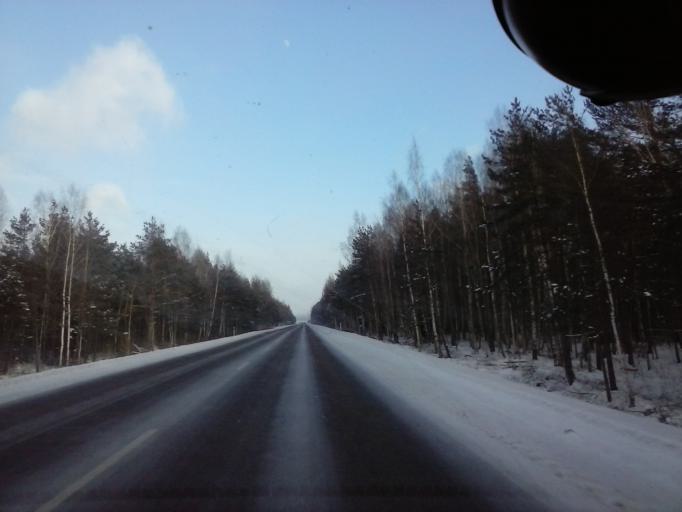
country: EE
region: Tartu
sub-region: Puhja vald
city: Puhja
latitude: 58.3270
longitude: 26.2407
